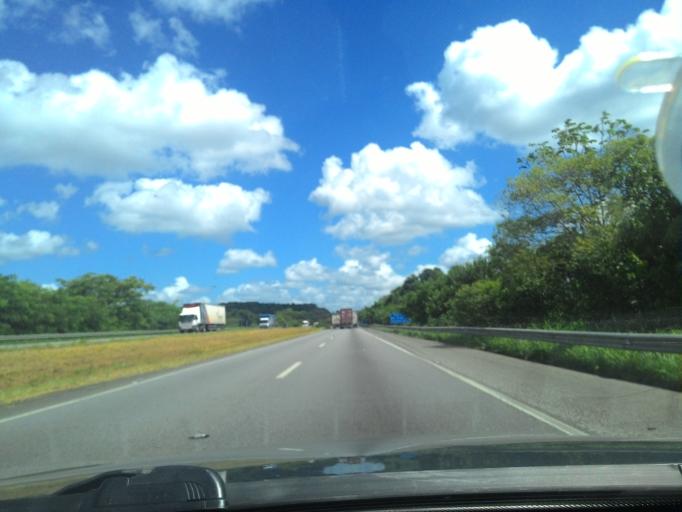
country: BR
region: Sao Paulo
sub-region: Registro
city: Registro
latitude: -24.5918
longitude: -47.8798
